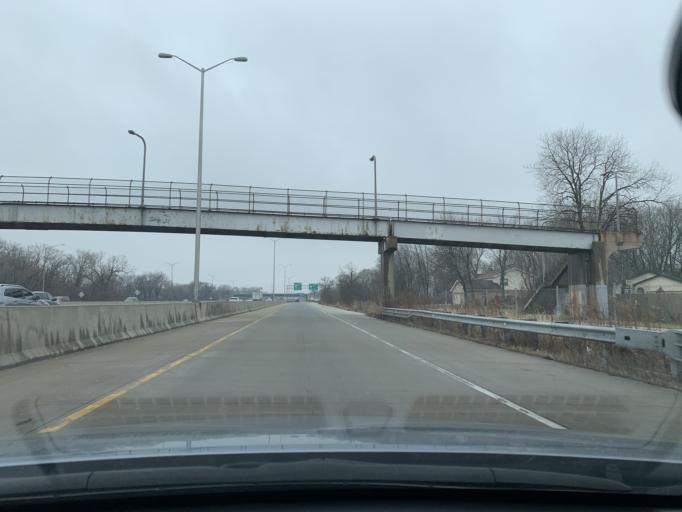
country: US
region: Illinois
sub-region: Cook County
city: Markham
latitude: 41.6053
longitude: -87.7048
